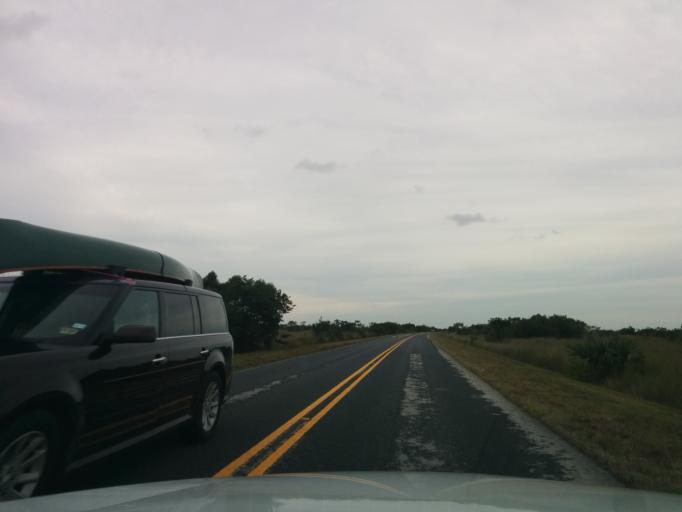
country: US
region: Florida
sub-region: Miami-Dade County
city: Florida City
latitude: 25.4329
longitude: -80.7365
